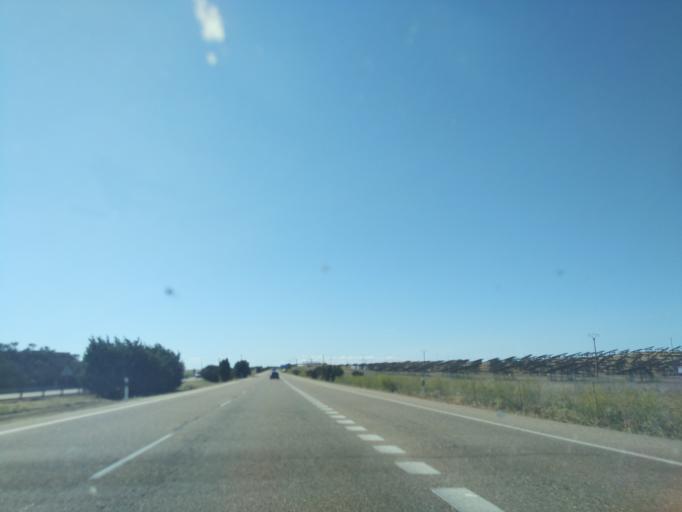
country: ES
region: Castille and Leon
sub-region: Provincia de Zamora
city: Villalpando
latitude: 41.8706
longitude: -5.4368
